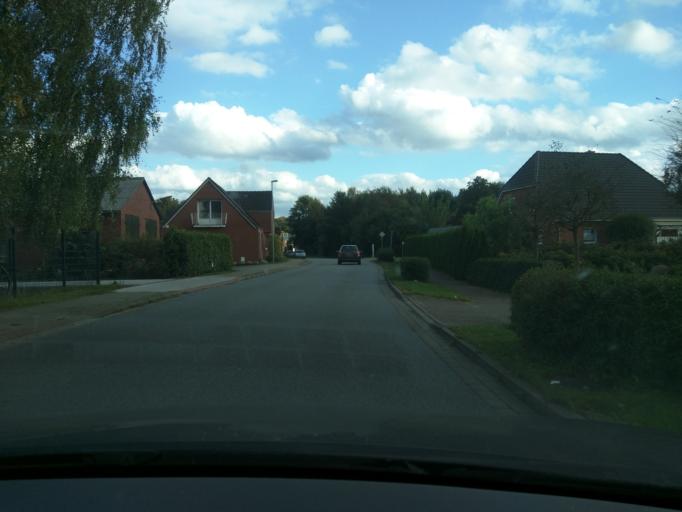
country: DE
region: Lower Saxony
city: Marschacht
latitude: 53.4112
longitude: 10.3856
